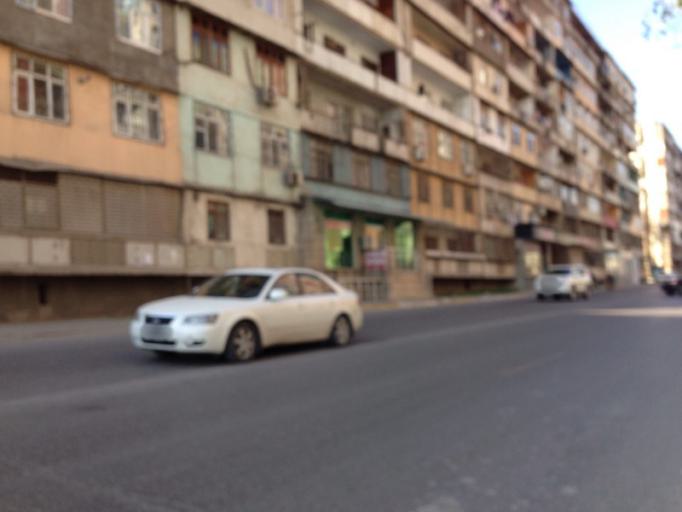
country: AZ
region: Baki
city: Baku
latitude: 40.4058
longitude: 49.8756
